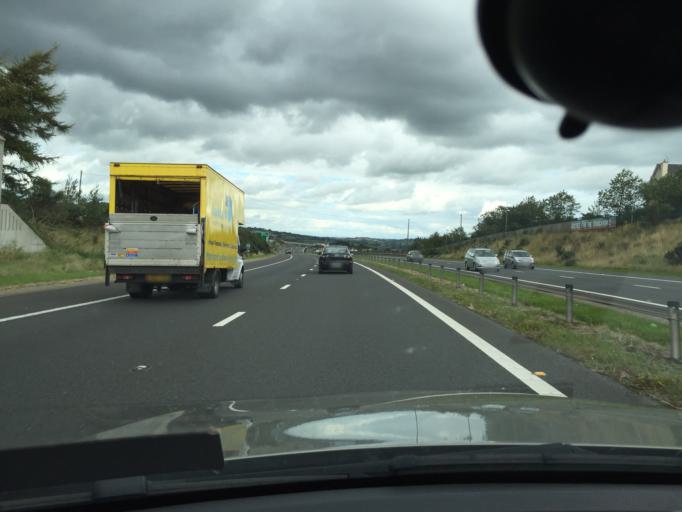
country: GB
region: Northern Ireland
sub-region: Newry and Mourne District
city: Newry
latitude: 54.1783
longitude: -6.3597
